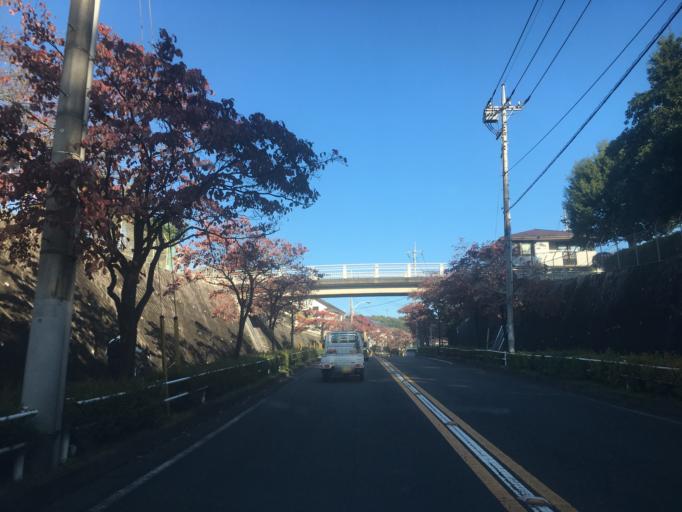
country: JP
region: Tokyo
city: Hino
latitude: 35.6838
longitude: 139.3585
